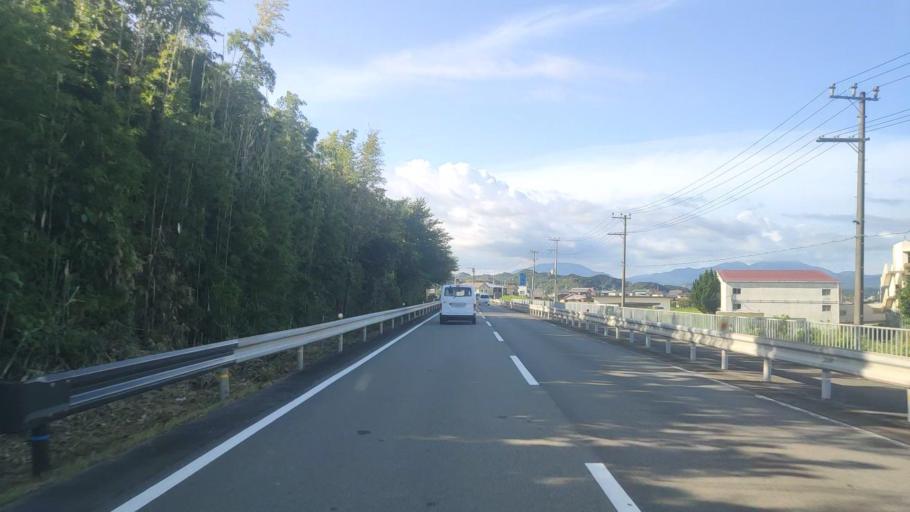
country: JP
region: Wakayama
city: Tanabe
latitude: 33.6733
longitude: 135.4079
